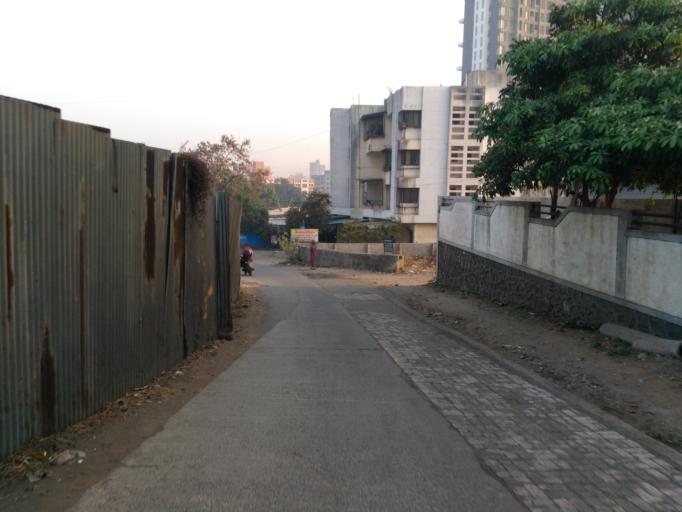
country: IN
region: Maharashtra
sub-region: Pune Division
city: Pune
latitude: 18.4489
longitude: 73.8795
